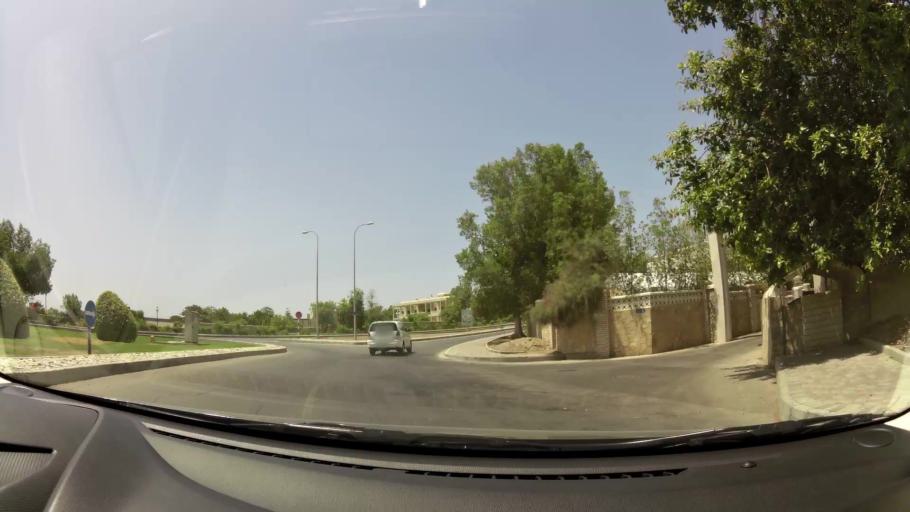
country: OM
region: Muhafazat Masqat
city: Muscat
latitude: 23.6301
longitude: 58.4836
